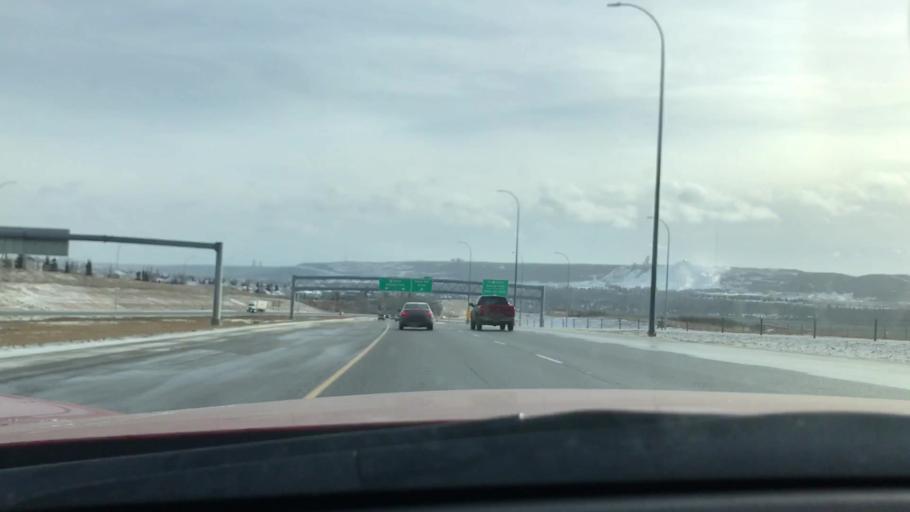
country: CA
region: Alberta
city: Calgary
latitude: 51.1146
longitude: -114.2283
